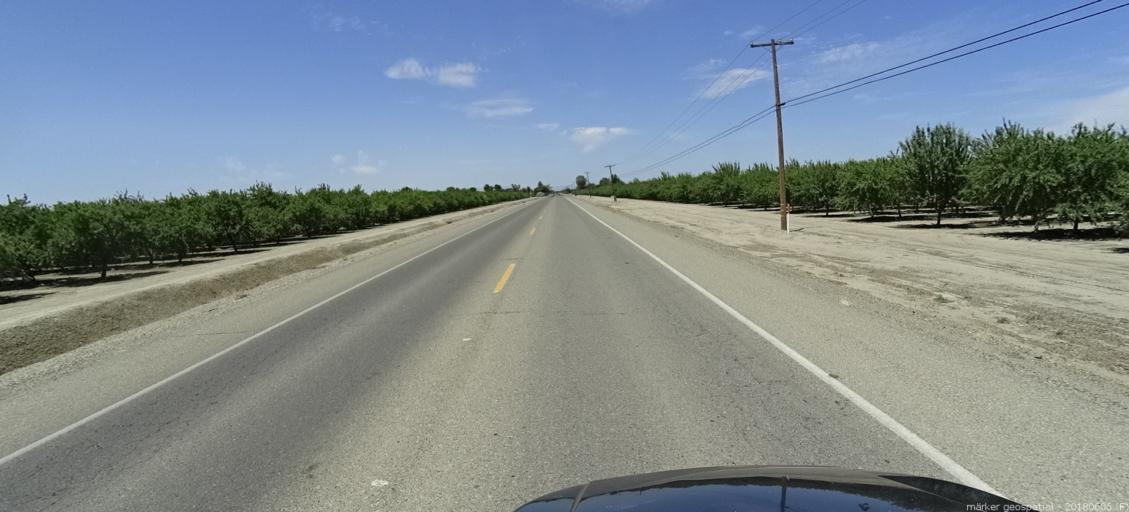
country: US
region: California
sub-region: Fresno County
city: Firebaugh
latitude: 36.8584
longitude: -120.4122
